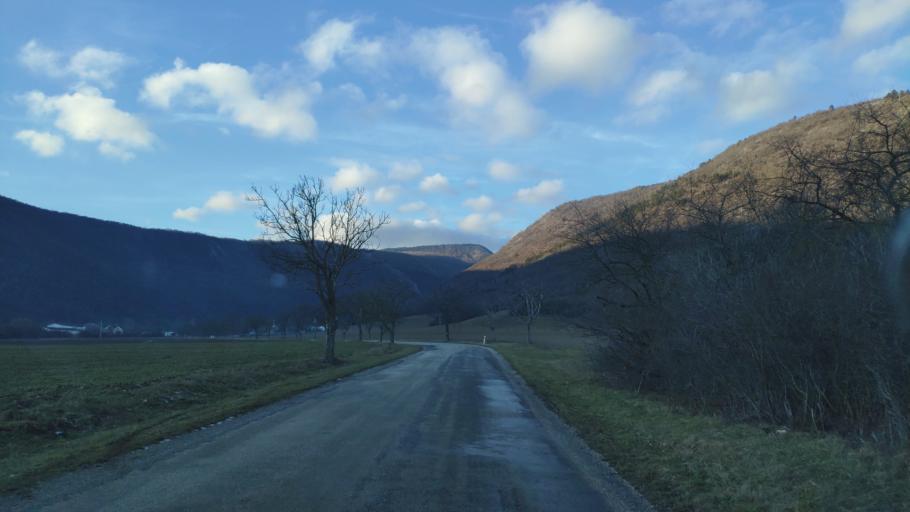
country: SK
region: Kosicky
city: Medzev
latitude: 48.6225
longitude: 20.8672
